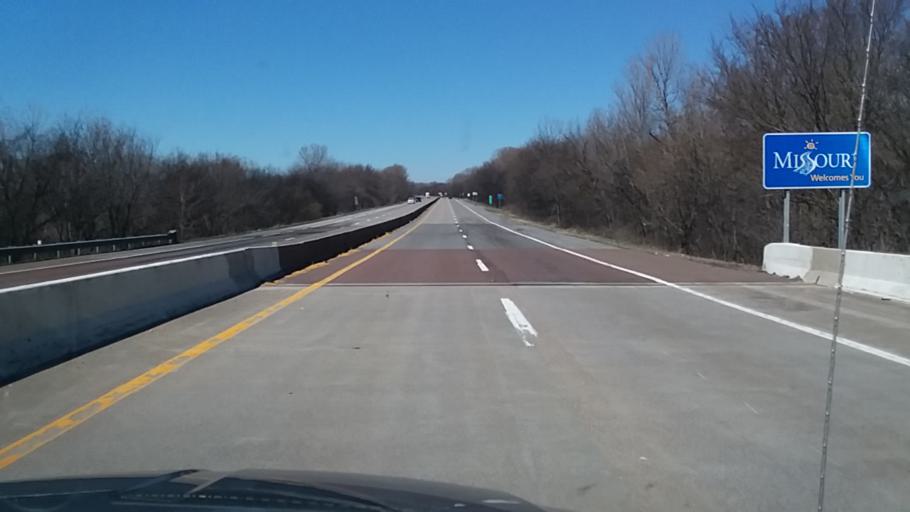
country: US
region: Missouri
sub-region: Pemiscot County
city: Caruthersville
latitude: 36.1207
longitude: -89.6163
